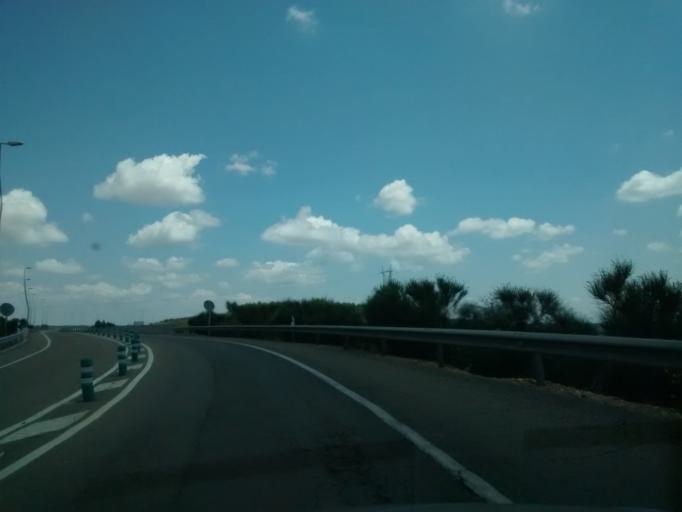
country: ES
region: Castille and Leon
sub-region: Provincia de Leon
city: Astorga
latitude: 42.4357
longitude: -6.0510
